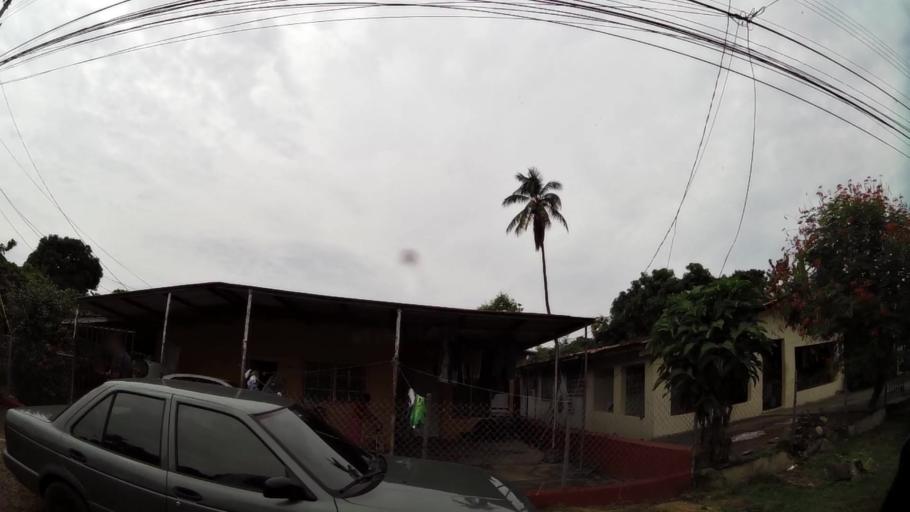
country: PA
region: Panama
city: San Miguelito
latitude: 9.0412
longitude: -79.4396
